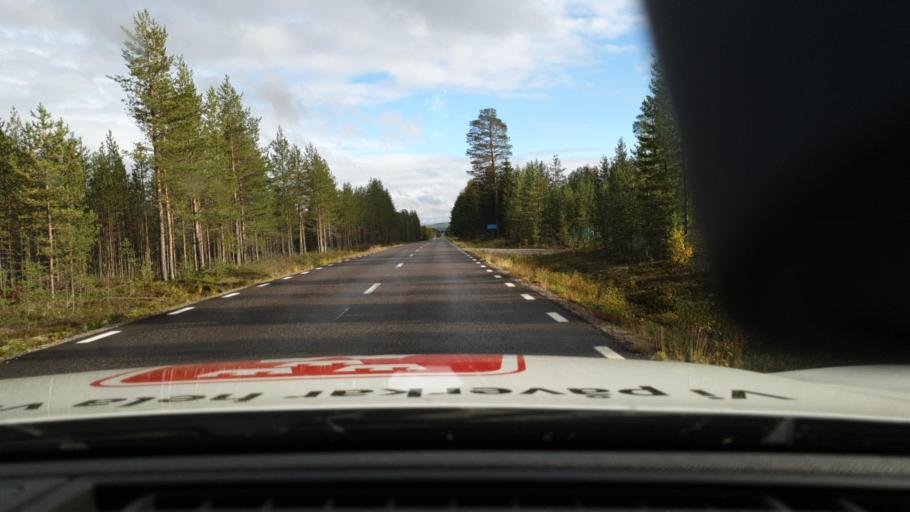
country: SE
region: Norrbotten
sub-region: Overkalix Kommun
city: OEverkalix
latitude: 66.9587
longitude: 22.6945
